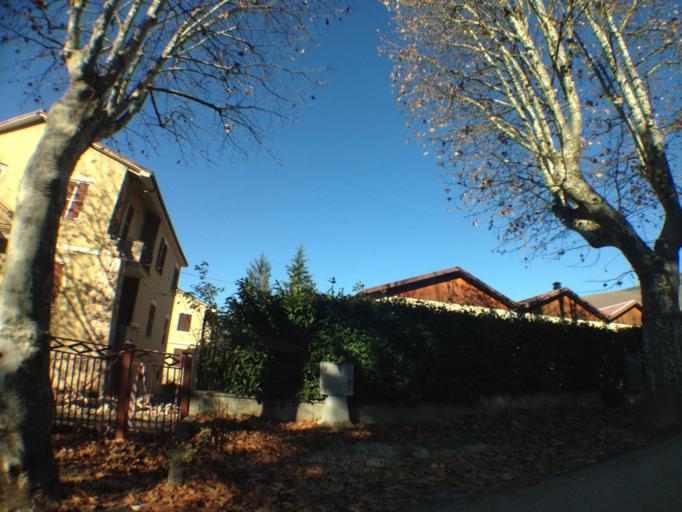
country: IT
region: Umbria
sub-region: Provincia di Perugia
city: Norcia
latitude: 42.7966
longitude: 13.0932
